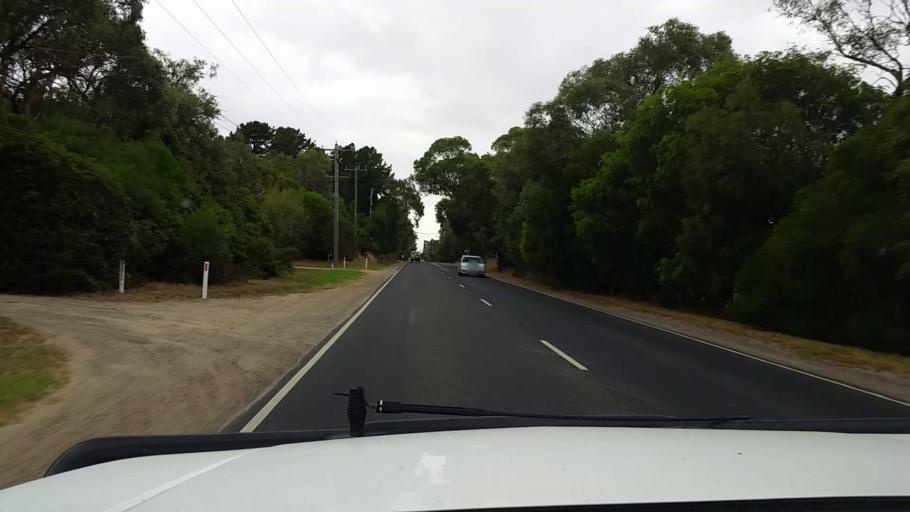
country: AU
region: Victoria
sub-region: Mornington Peninsula
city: Langwarrin South
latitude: -38.1993
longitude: 145.1904
